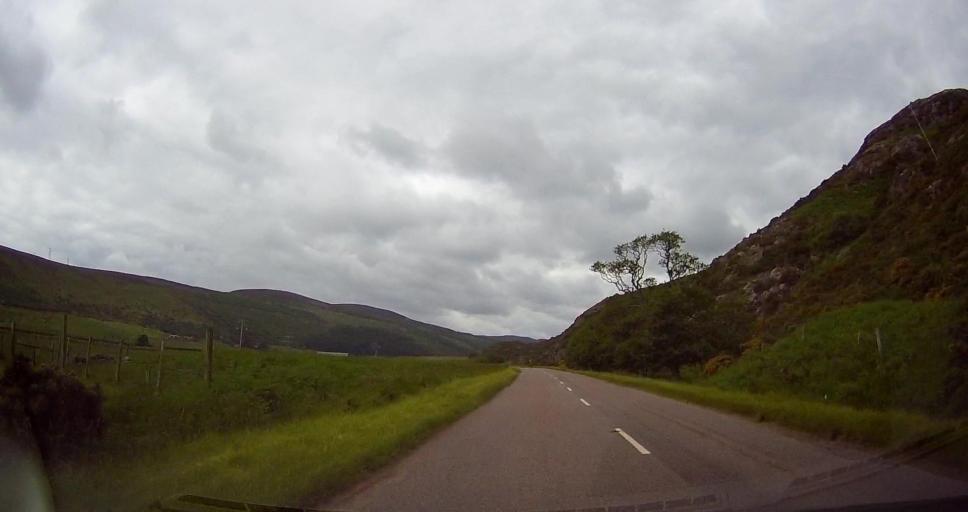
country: GB
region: Scotland
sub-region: Highland
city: Dornoch
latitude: 57.9823
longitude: -4.1213
